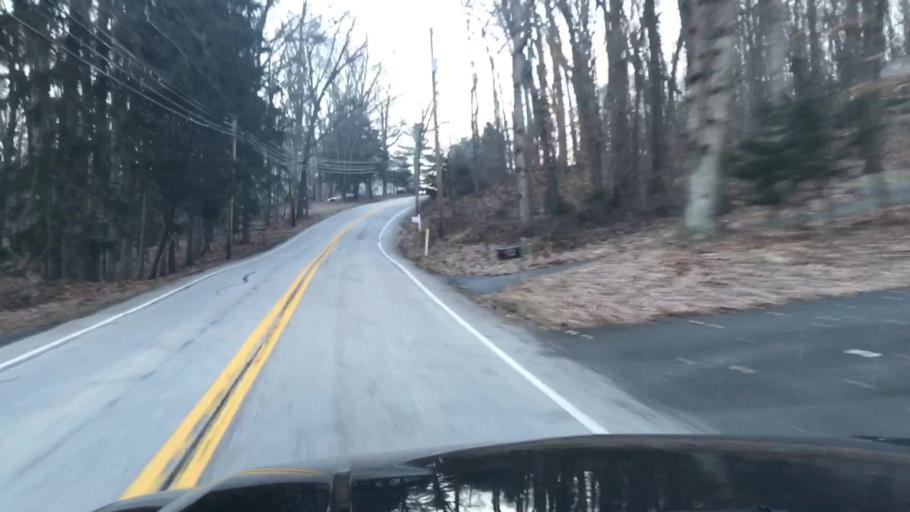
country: US
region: Pennsylvania
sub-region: Cumberland County
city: Lower Allen
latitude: 40.1774
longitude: -76.8865
